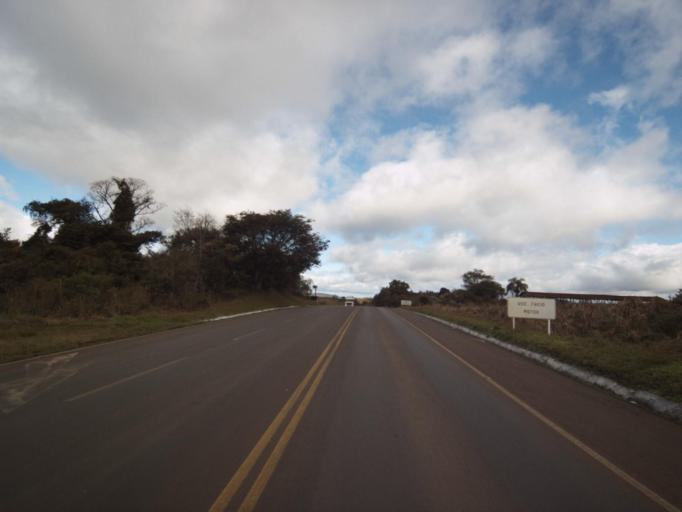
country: BR
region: Santa Catarina
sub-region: Concordia
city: Concordia
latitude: -27.1095
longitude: -51.9057
